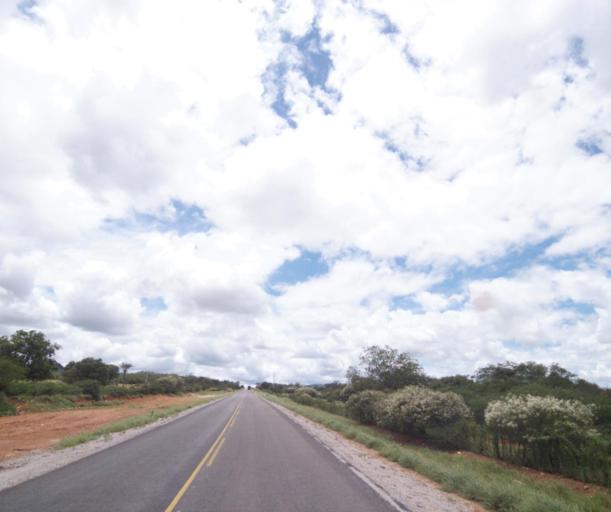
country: BR
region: Bahia
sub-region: Brumado
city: Brumado
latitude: -14.1506
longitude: -41.4980
